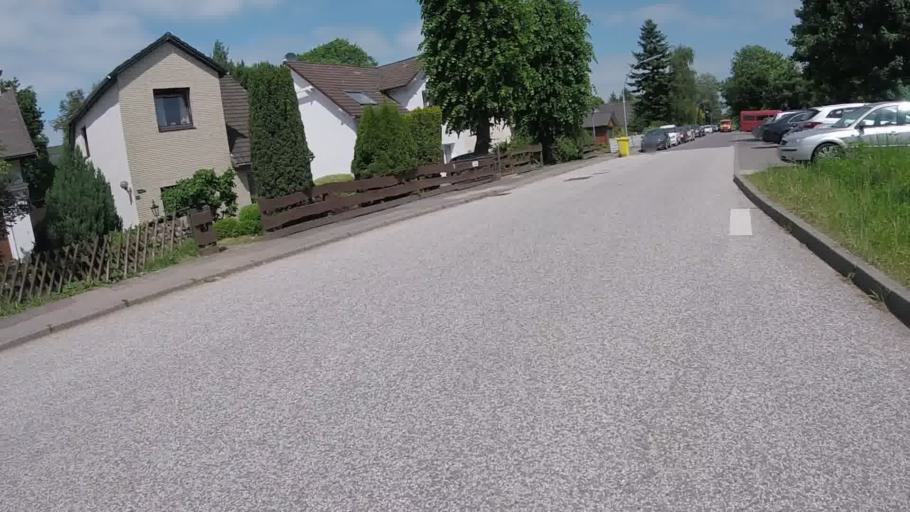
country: DE
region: Hamburg
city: Wandsbek
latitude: 53.5168
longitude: 10.0977
